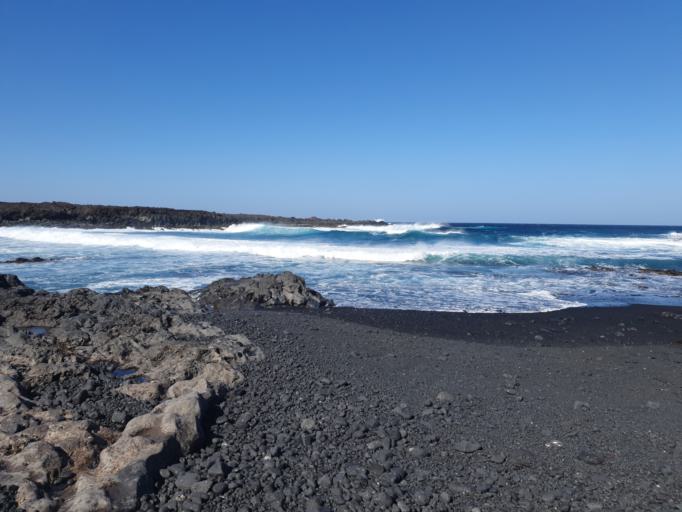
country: ES
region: Canary Islands
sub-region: Provincia de Las Palmas
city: Tinajo
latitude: 29.0637
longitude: -13.7660
